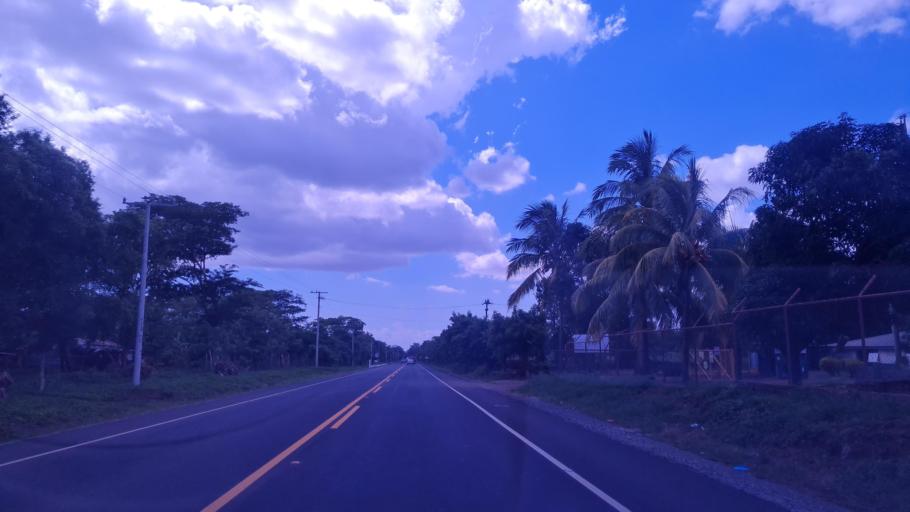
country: NI
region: Masaya
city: Nindiri
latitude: 12.0309
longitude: -86.1240
